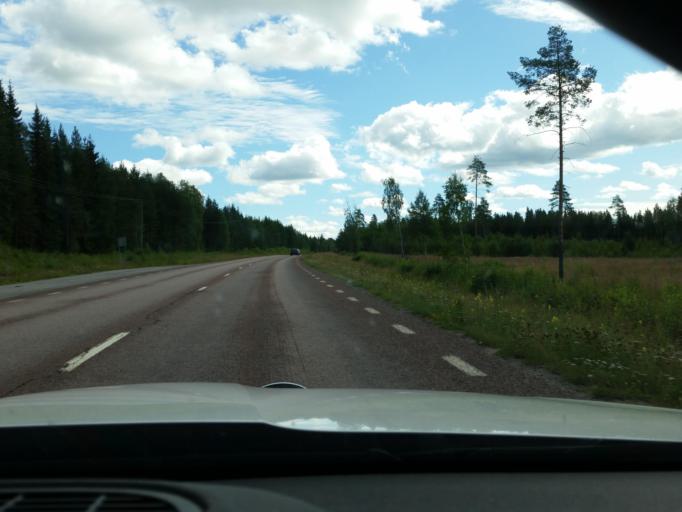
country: SE
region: Norrbotten
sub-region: Alvsbyns Kommun
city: AElvsbyn
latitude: 65.6717
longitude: 21.0685
